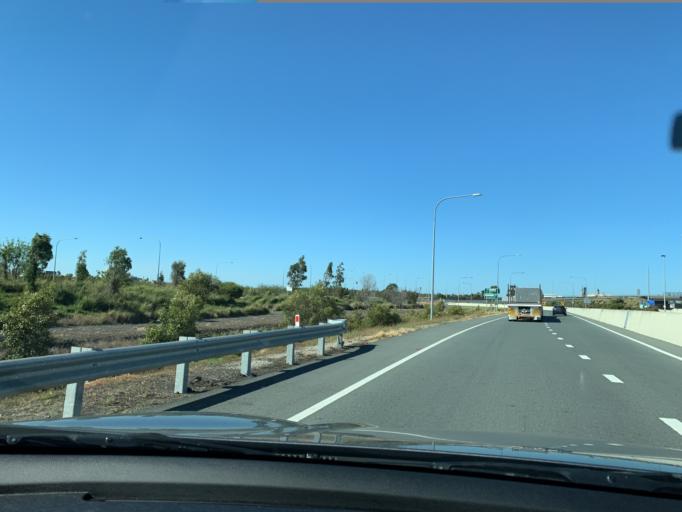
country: AU
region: Queensland
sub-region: Brisbane
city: Wynnum
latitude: -27.4277
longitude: 153.1444
